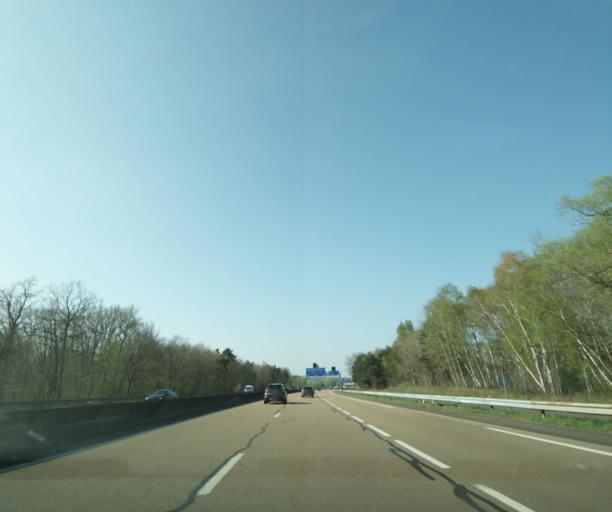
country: FR
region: Ile-de-France
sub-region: Departement de Seine-et-Marne
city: Arbonne-la-Foret
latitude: 48.4176
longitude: 2.5440
